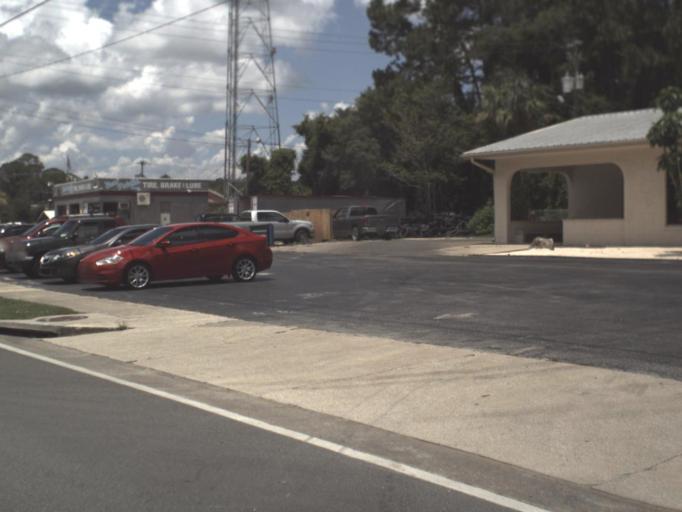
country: US
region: Florida
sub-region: Putnam County
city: East Palatka
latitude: 29.6440
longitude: -81.6062
